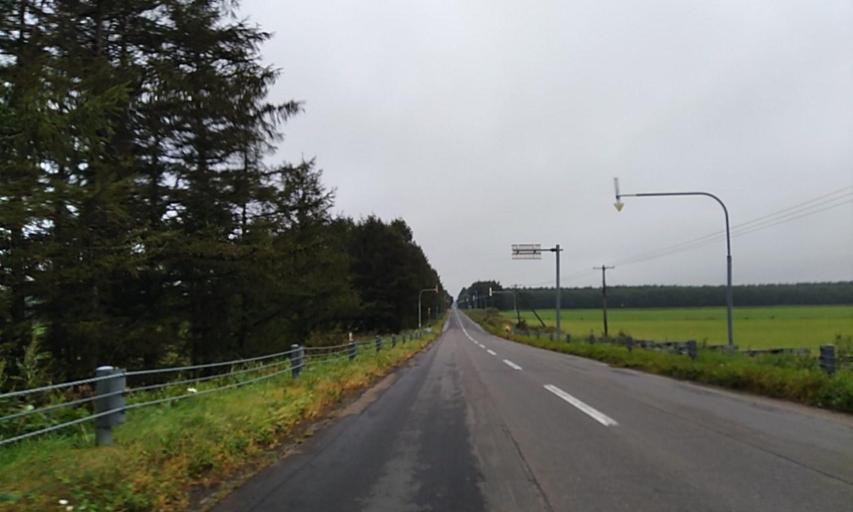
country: JP
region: Hokkaido
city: Shibetsu
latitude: 43.5053
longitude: 144.6623
